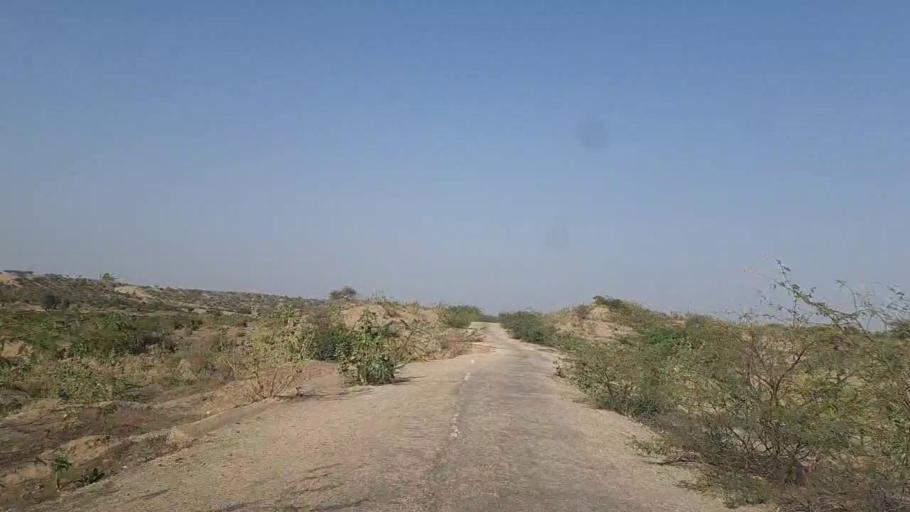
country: PK
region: Sindh
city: Naukot
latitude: 24.6231
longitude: 69.3514
